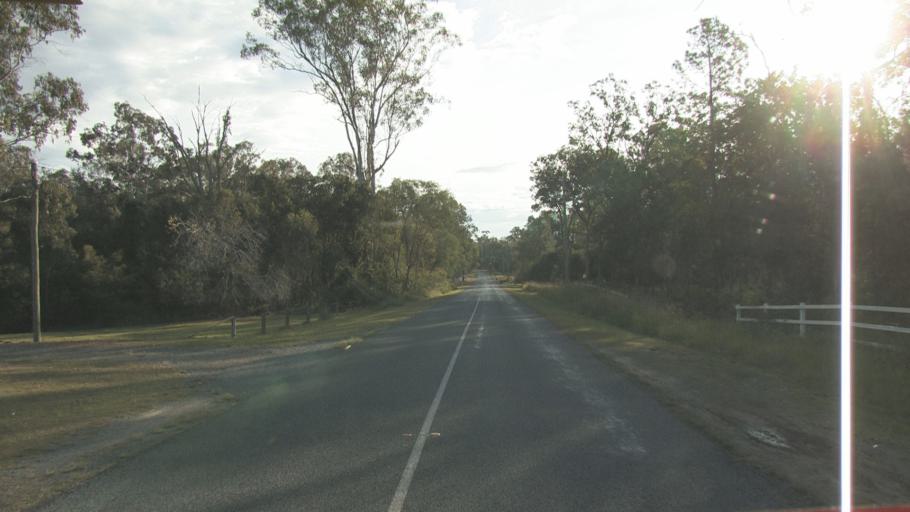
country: AU
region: Queensland
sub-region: Logan
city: Cedar Vale
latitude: -27.8481
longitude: 153.1072
